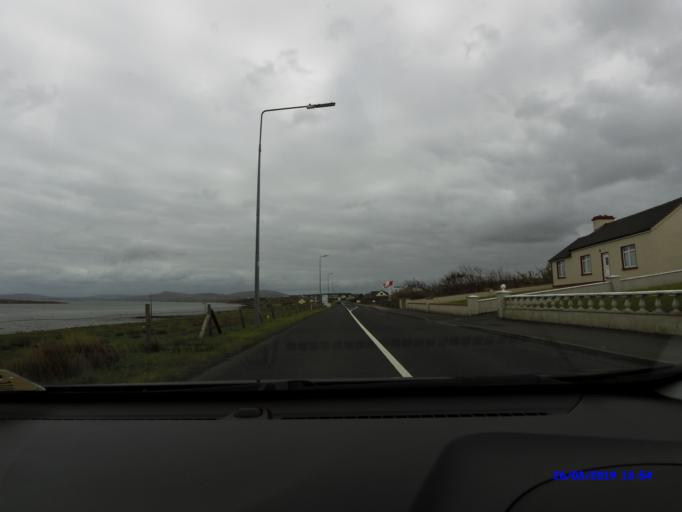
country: IE
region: Connaught
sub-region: Maigh Eo
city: Belmullet
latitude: 54.2197
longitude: -9.9766
